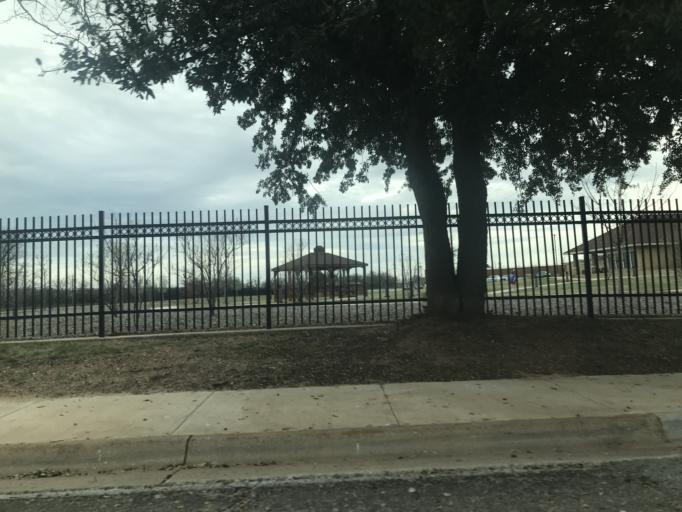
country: US
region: Texas
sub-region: Taylor County
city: Abilene
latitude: 32.4685
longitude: -99.7289
